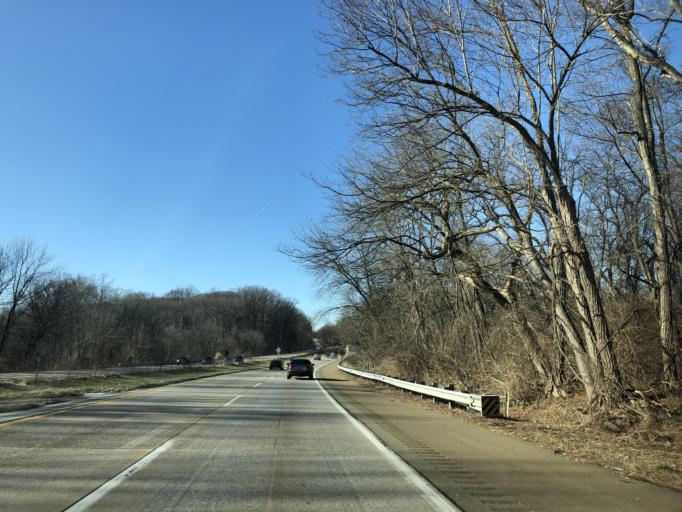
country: US
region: Pennsylvania
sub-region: Chester County
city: Kennett Square
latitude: 39.8567
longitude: -75.7066
